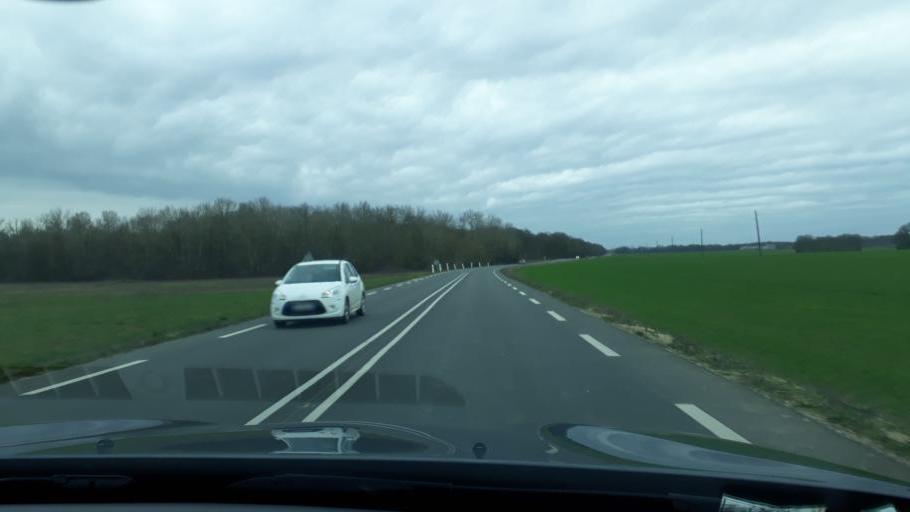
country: FR
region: Centre
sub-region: Departement du Loiret
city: Chanteau
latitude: 48.0279
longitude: 1.9714
